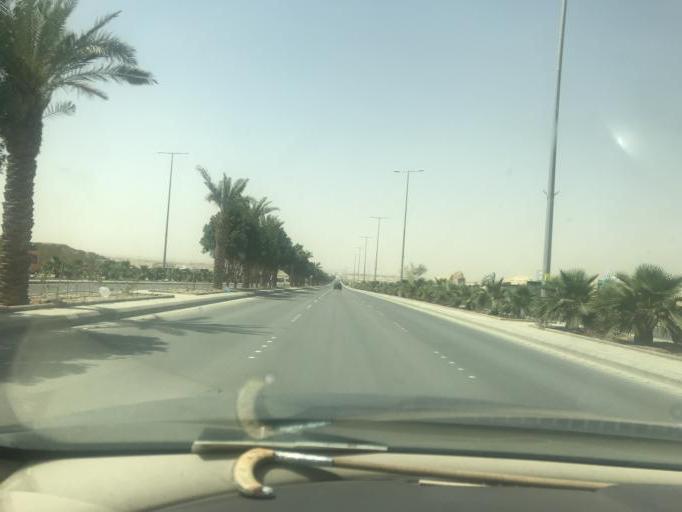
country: SA
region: Ar Riyad
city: Riyadh
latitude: 24.7983
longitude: 46.5849
